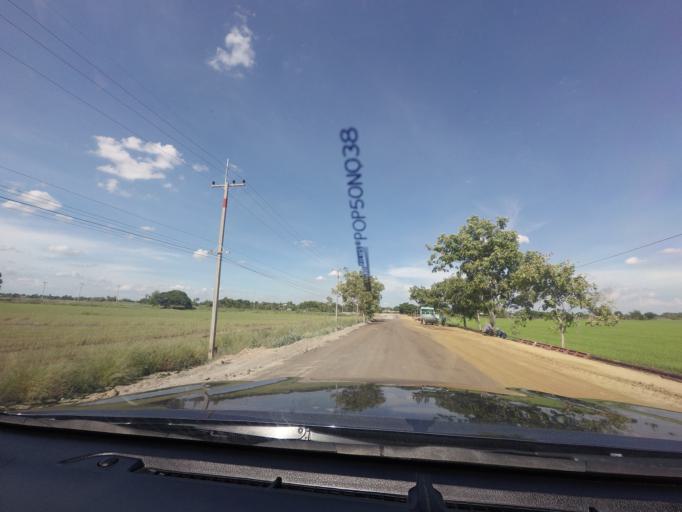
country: TH
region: Suphan Buri
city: Song Phi Nong
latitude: 14.1795
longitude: 100.0424
